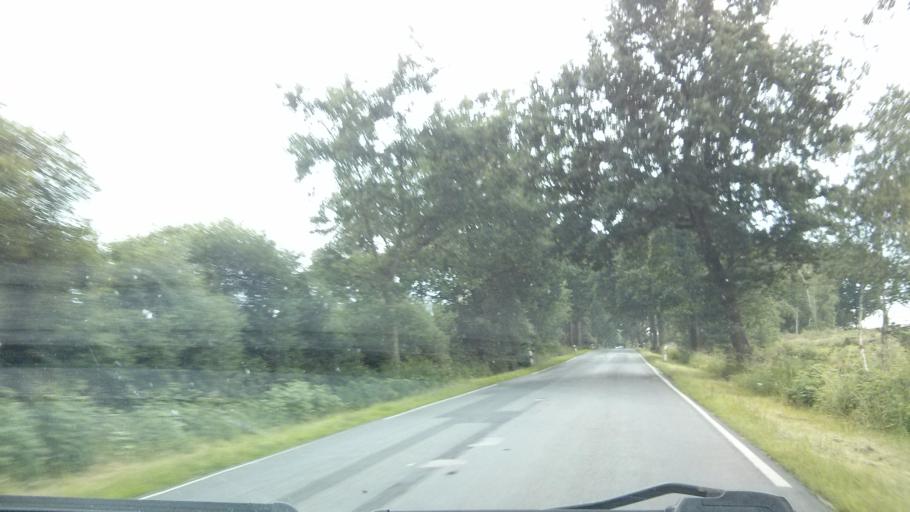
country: DE
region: Lower Saxony
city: Beverstedt
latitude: 53.4638
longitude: 8.8446
